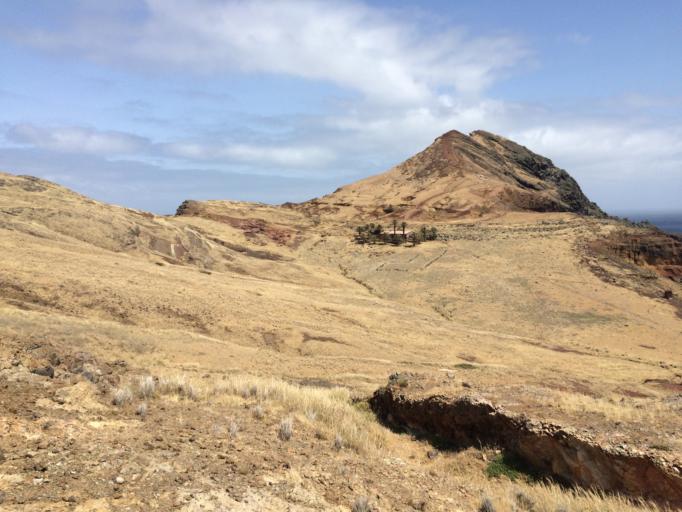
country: PT
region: Madeira
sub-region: Machico
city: Canical
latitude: 32.7444
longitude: -16.6863
